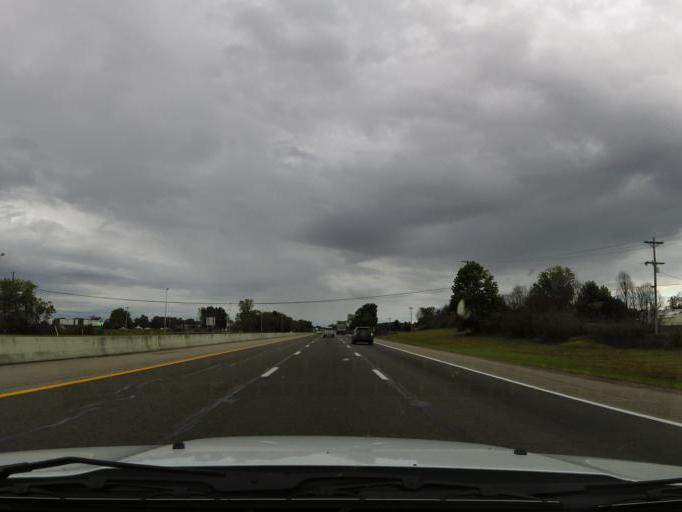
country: US
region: Kentucky
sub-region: Laurel County
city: London
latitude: 37.0490
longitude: -84.0987
